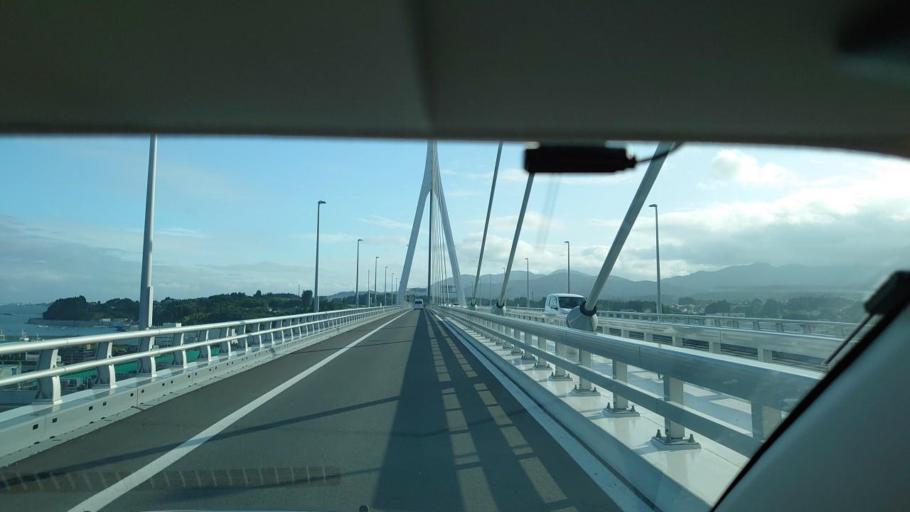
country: JP
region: Iwate
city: Ofunato
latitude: 38.8927
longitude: 141.5923
